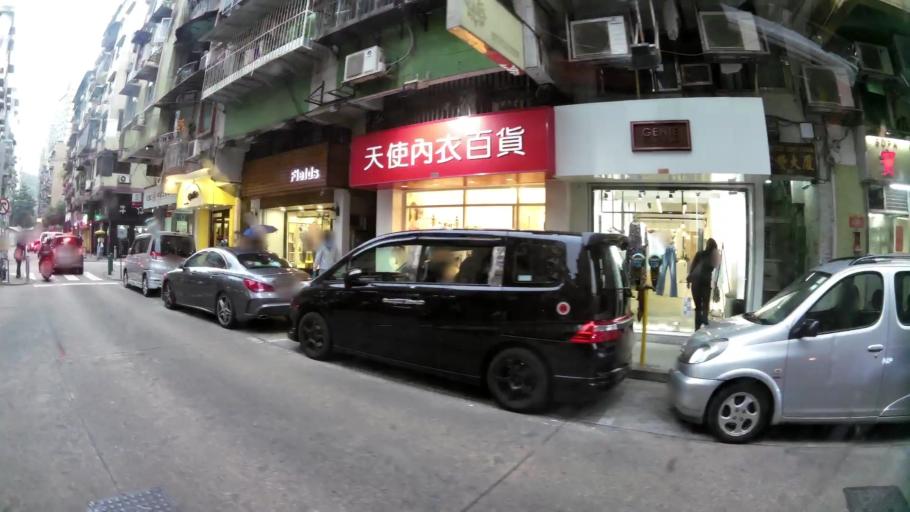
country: MO
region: Macau
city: Macau
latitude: 22.2013
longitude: 113.5461
